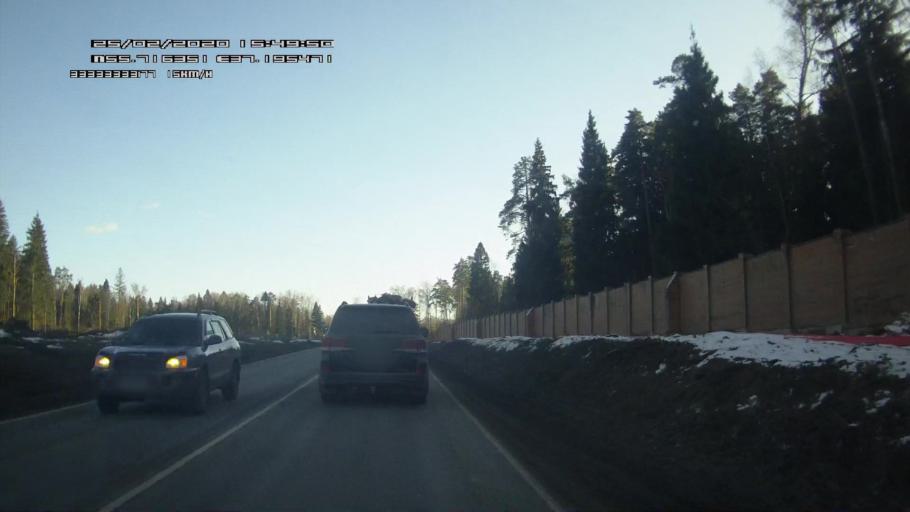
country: RU
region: Moskovskaya
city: Gorki Vtoryye
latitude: 55.7164
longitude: 37.1954
